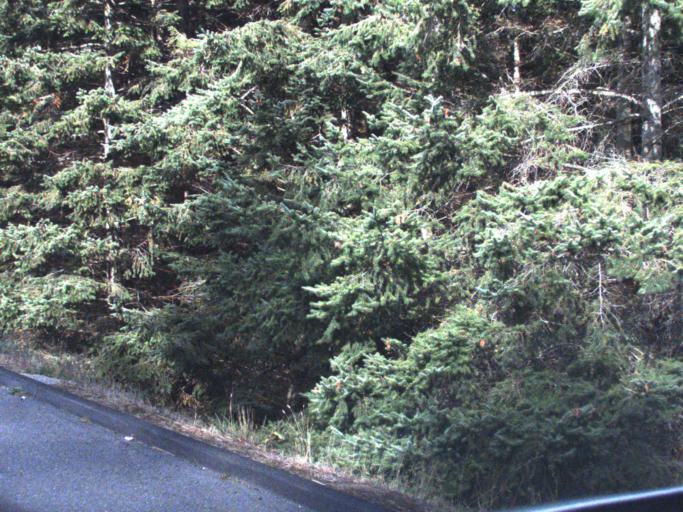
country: US
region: Washington
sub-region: Island County
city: Coupeville
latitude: 48.2242
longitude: -122.7370
